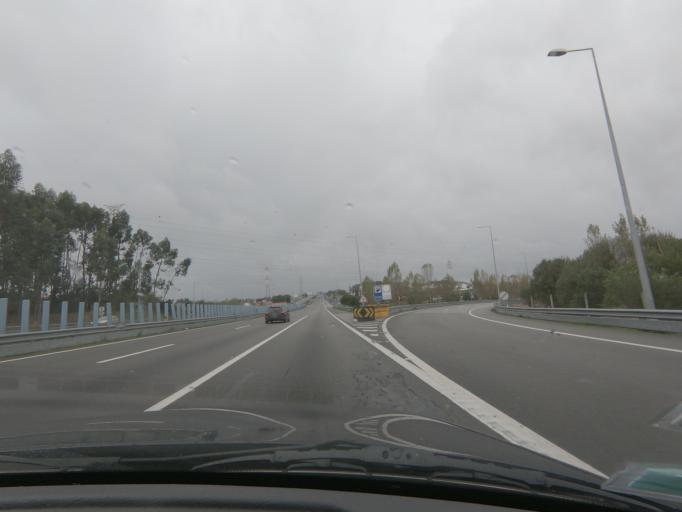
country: PT
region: Porto
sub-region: Maia
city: Leca do Bailio
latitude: 41.2028
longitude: -8.6180
